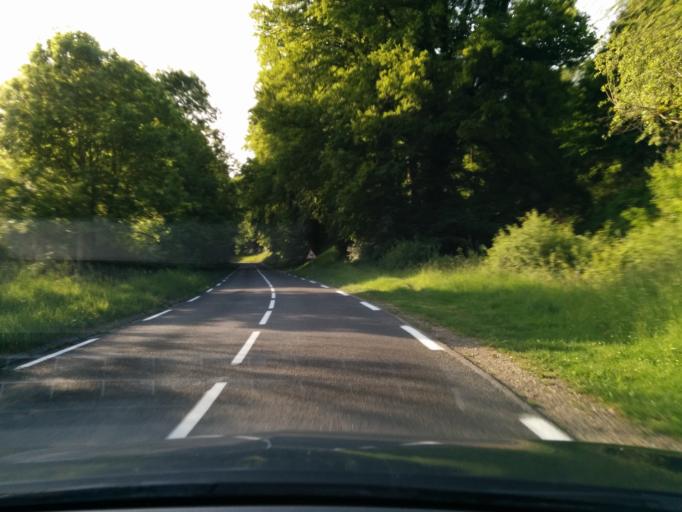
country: FR
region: Haute-Normandie
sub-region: Departement de la Seine-Maritime
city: La Feuillie
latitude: 49.4069
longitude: 1.4827
